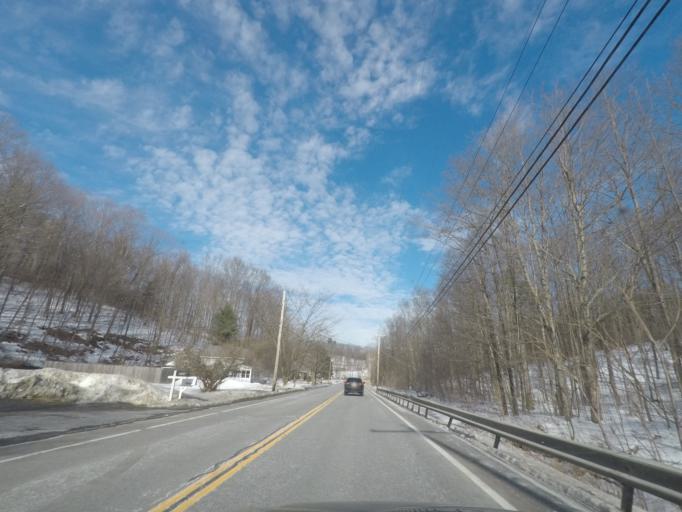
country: US
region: New York
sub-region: Albany County
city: Altamont
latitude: 42.7743
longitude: -74.0789
